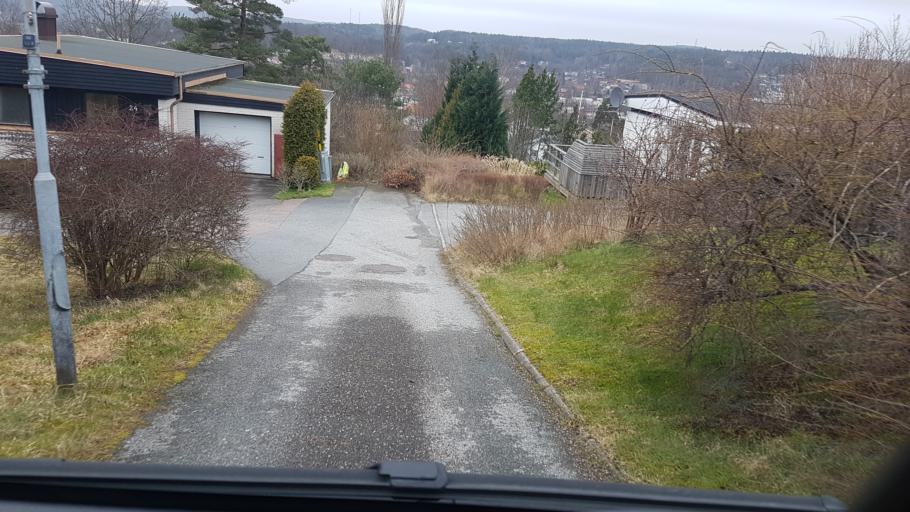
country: SE
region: Vaestra Goetaland
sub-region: Lerums Kommun
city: Lerum
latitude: 57.7671
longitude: 12.2772
